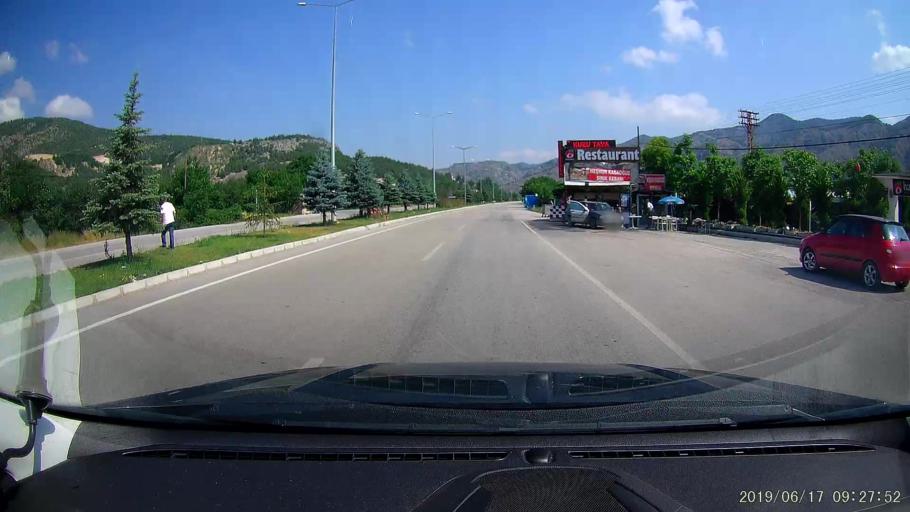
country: TR
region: Amasya
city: Amasya
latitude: 40.6819
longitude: 35.8239
